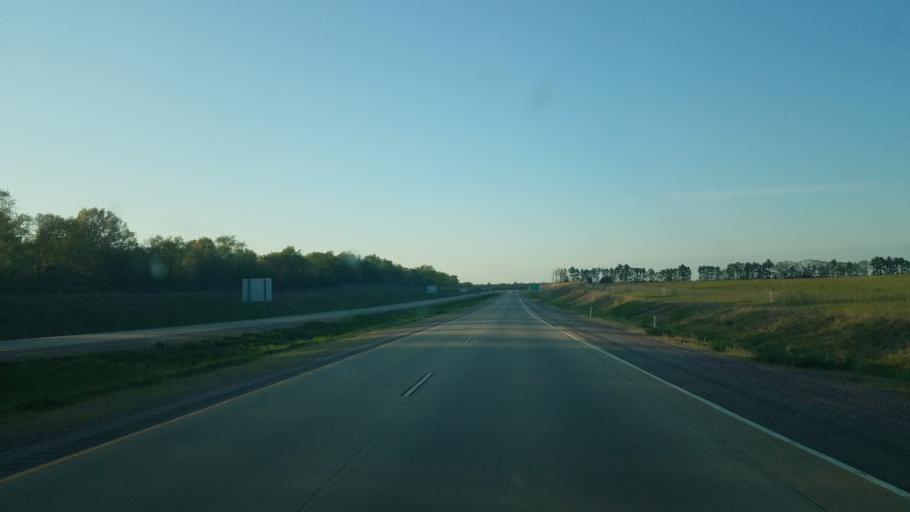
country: US
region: Wisconsin
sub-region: Sauk County
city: Lake Delton
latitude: 43.5383
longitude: -89.7870
